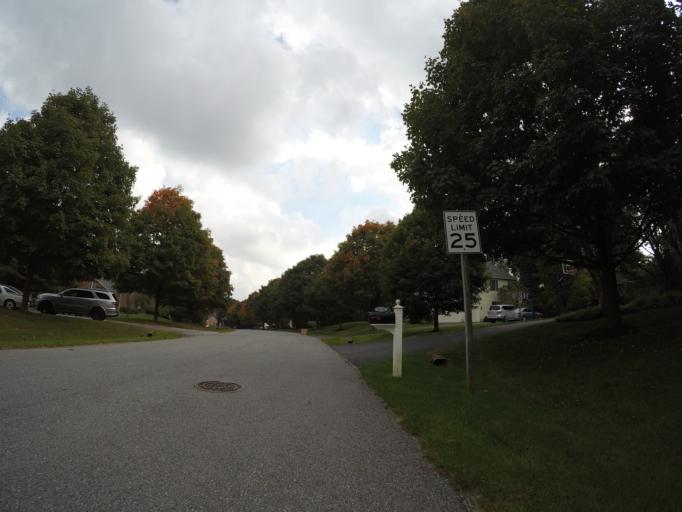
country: US
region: Maryland
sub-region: Howard County
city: Columbia
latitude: 39.2642
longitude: -76.8747
